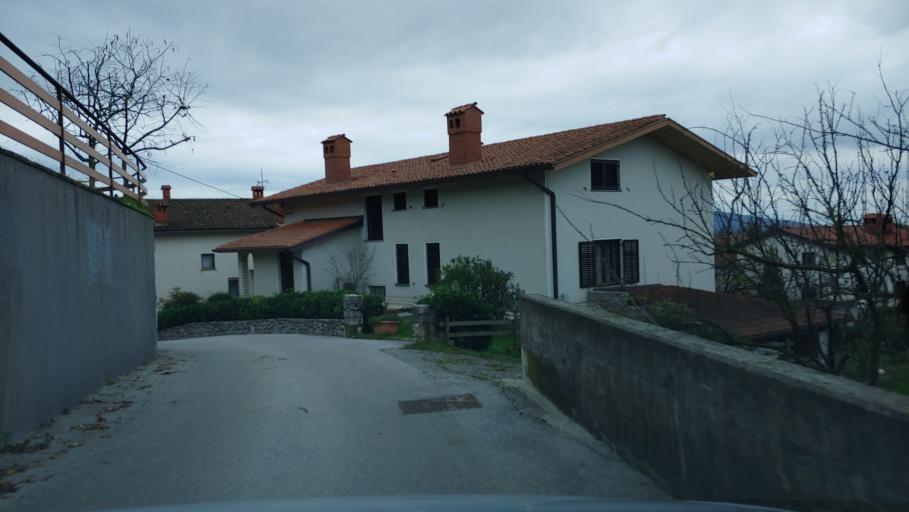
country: SI
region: Sempeter-Vrtojba
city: Vrtojba
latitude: 45.9165
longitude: 13.6417
